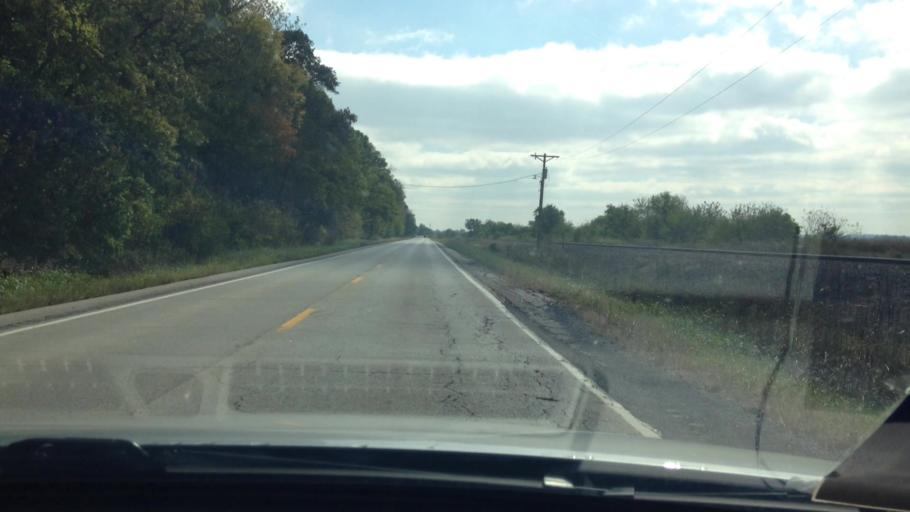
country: US
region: Kansas
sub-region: Leavenworth County
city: Lansing
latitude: 39.2918
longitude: -94.8410
